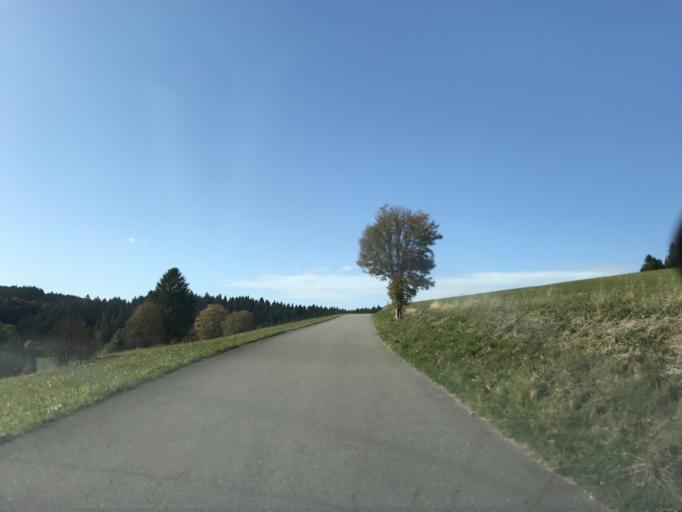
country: DE
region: Baden-Wuerttemberg
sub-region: Freiburg Region
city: Herrischried
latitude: 47.6737
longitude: 7.9834
